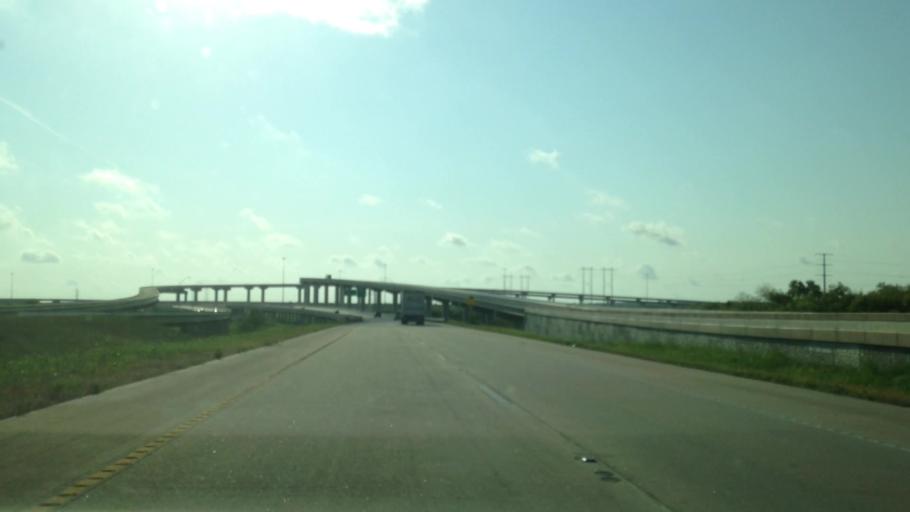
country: US
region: Texas
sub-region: Travis County
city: Onion Creek
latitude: 30.0809
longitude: -97.7033
